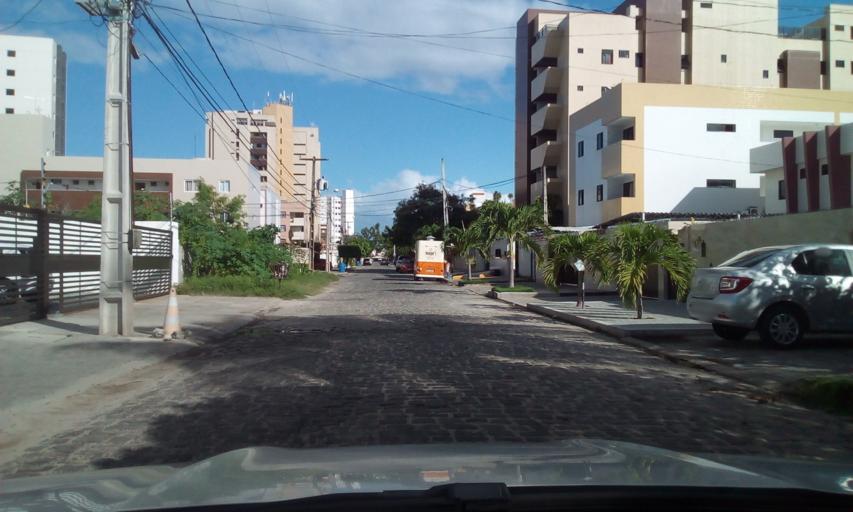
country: BR
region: Paraiba
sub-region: Joao Pessoa
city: Joao Pessoa
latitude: -7.0728
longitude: -34.8367
